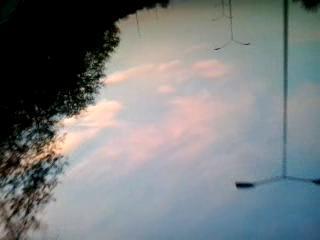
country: IT
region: Lombardy
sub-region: Provincia di Brescia
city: Roncadelle
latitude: 45.5343
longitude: 10.1795
